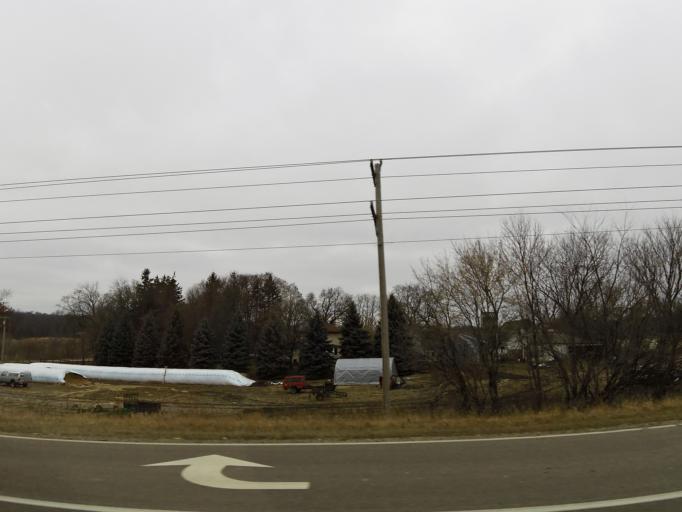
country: US
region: Minnesota
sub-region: Scott County
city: Prior Lake
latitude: 44.7469
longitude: -93.4283
